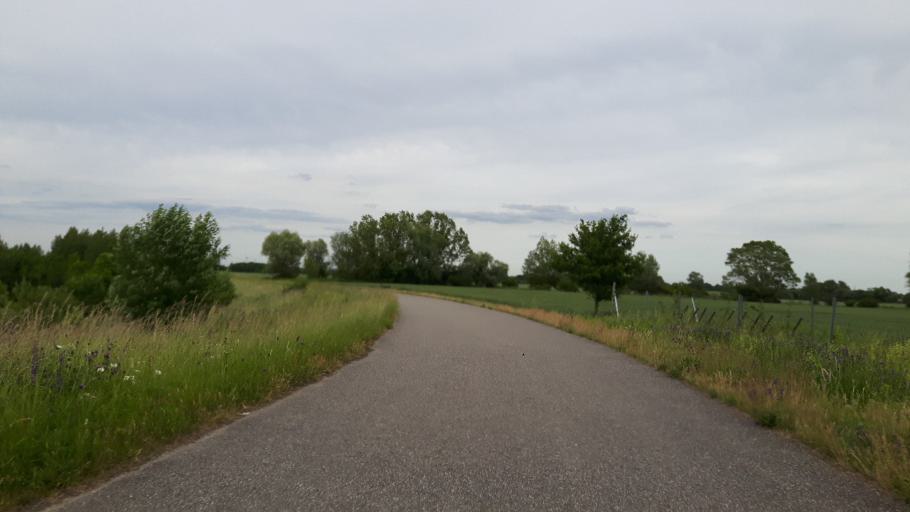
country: DE
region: Saxony
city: Rackwitz
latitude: 51.4299
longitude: 12.3350
